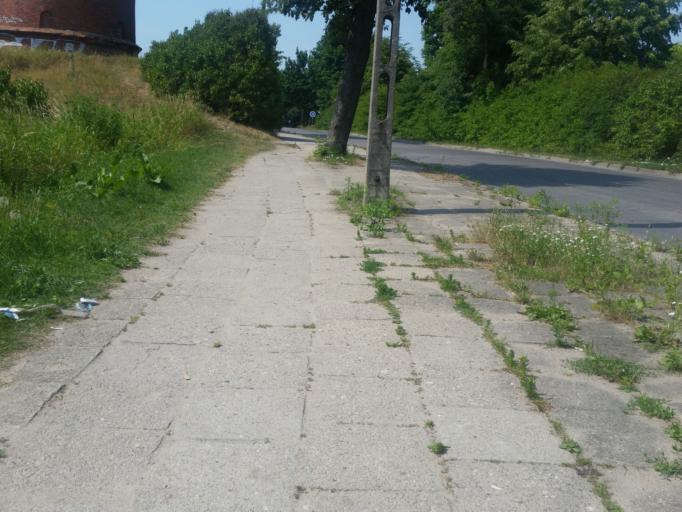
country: PL
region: Warmian-Masurian Voivodeship
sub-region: Powiat goldapski
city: Goldap
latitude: 54.3144
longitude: 22.3129
